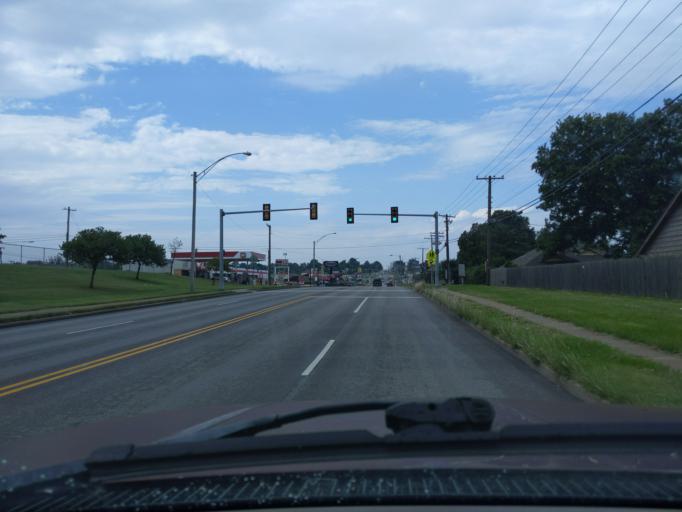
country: US
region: Oklahoma
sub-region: Tulsa County
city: Tulsa
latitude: 36.1335
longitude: -95.8991
